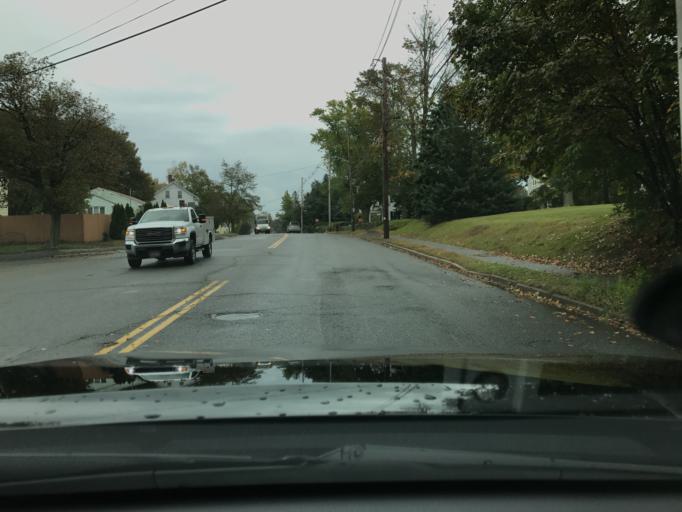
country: US
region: Massachusetts
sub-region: Essex County
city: Peabody
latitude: 42.5317
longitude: -70.9421
